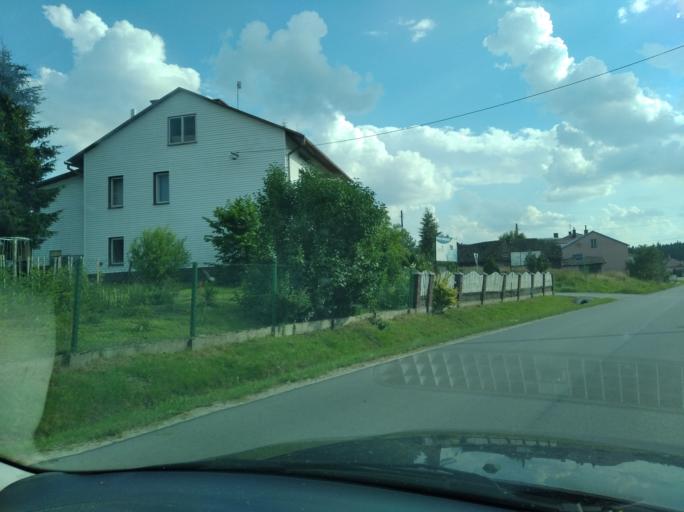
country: PL
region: Subcarpathian Voivodeship
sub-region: Powiat rzeszowski
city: Wysoka Glogowska
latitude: 50.1542
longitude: 22.0196
